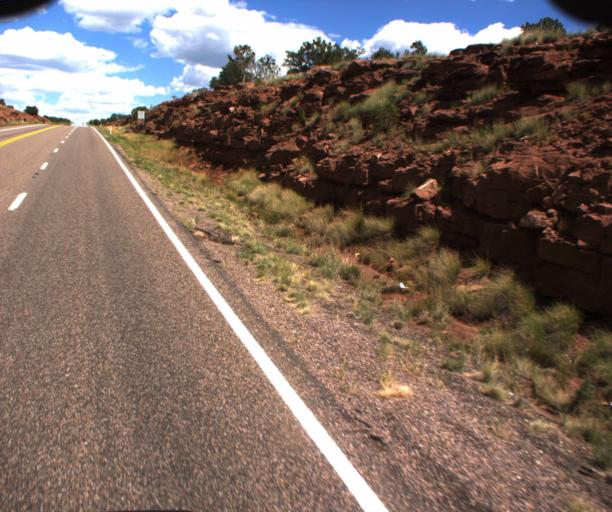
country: US
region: Arizona
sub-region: Apache County
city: Springerville
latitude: 34.1579
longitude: -109.1096
